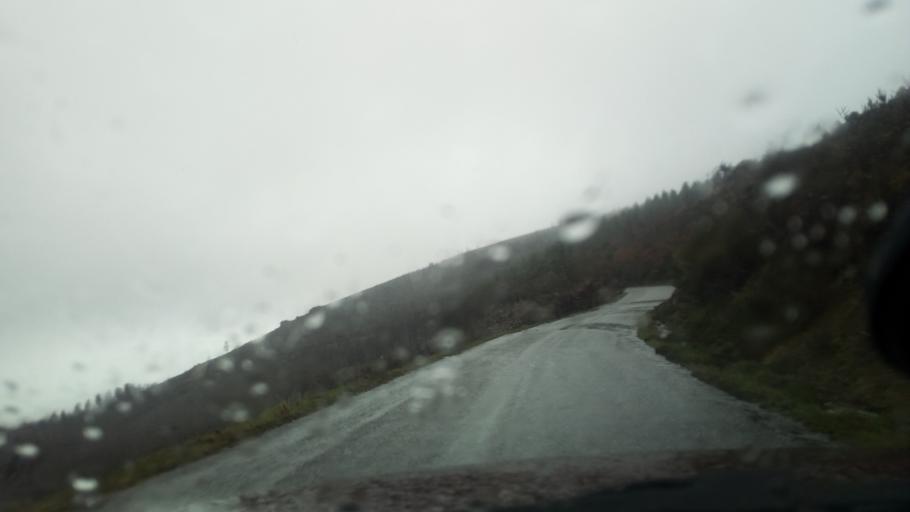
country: PT
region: Guarda
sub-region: Celorico da Beira
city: Celorico da Beira
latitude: 40.5360
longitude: -7.4459
